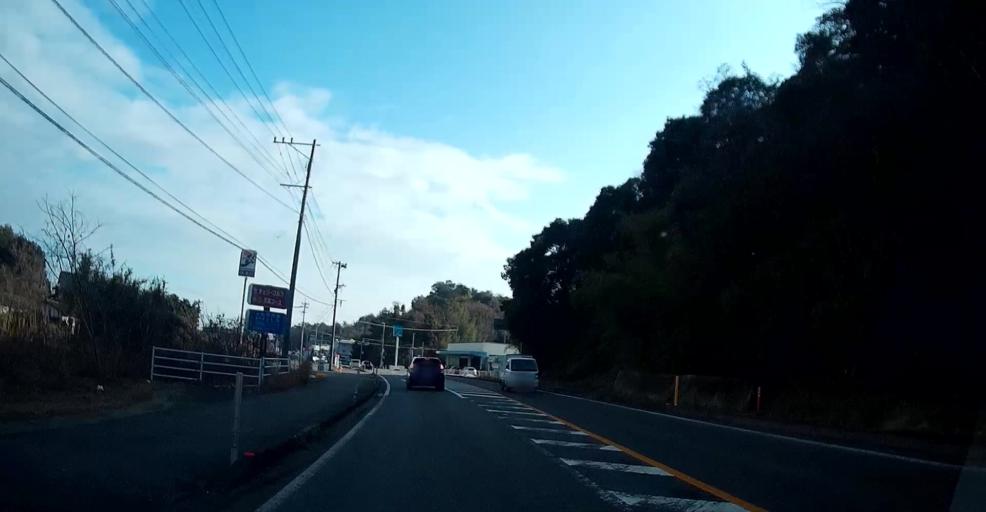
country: JP
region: Kumamoto
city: Yatsushiro
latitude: 32.5535
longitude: 130.4172
